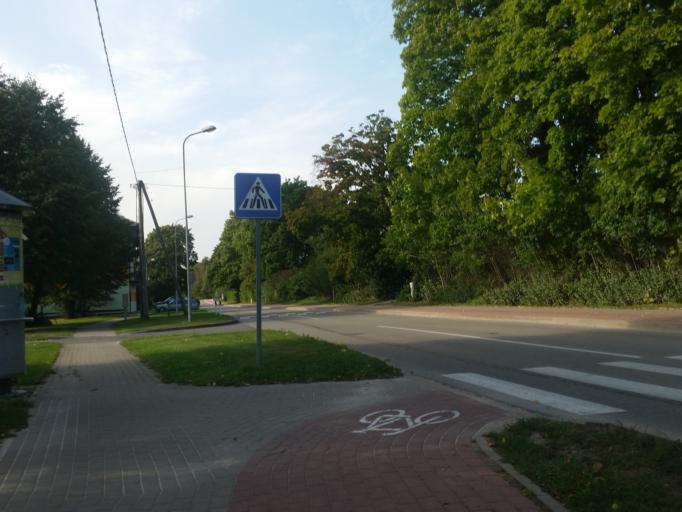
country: LV
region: Ikskile
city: Ikskile
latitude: 56.8224
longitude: 24.5003
